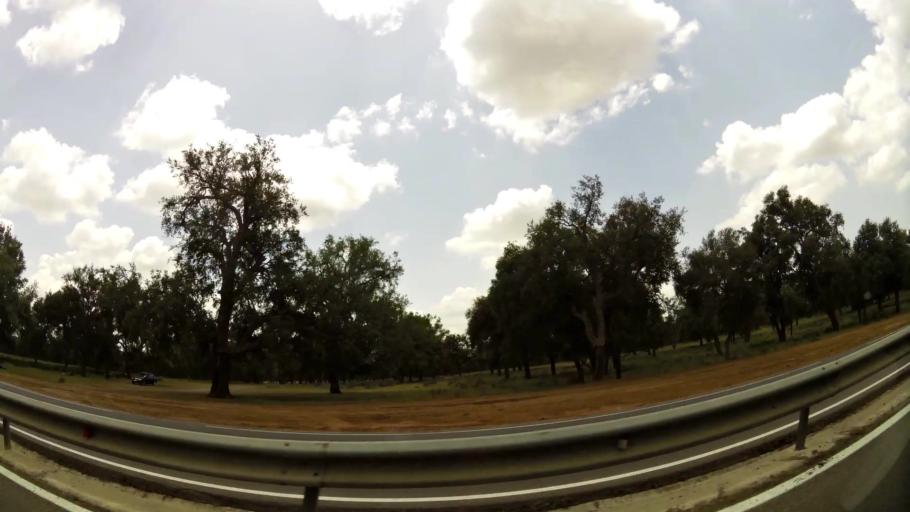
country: MA
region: Rabat-Sale-Zemmour-Zaer
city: Sale
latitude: 34.0200
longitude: -6.5757
